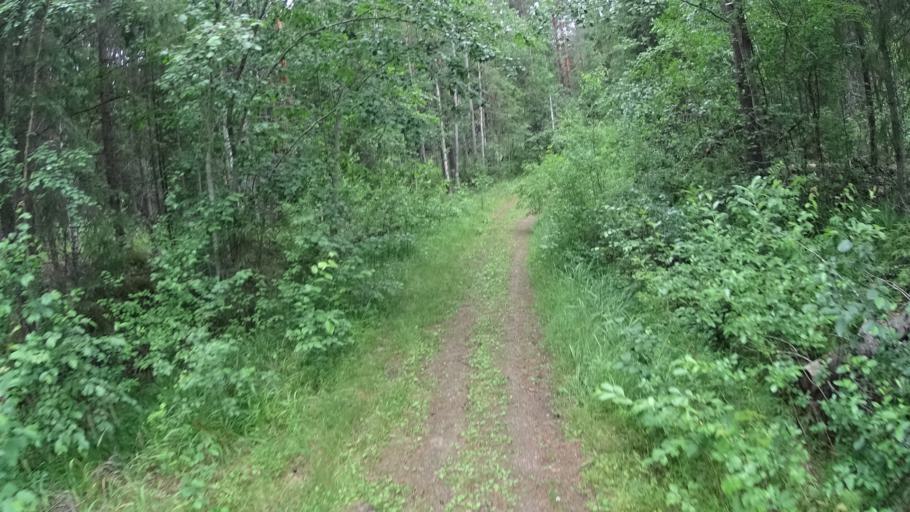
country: FI
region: Southern Savonia
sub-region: Mikkeli
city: Maentyharju
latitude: 61.1838
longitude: 26.8299
